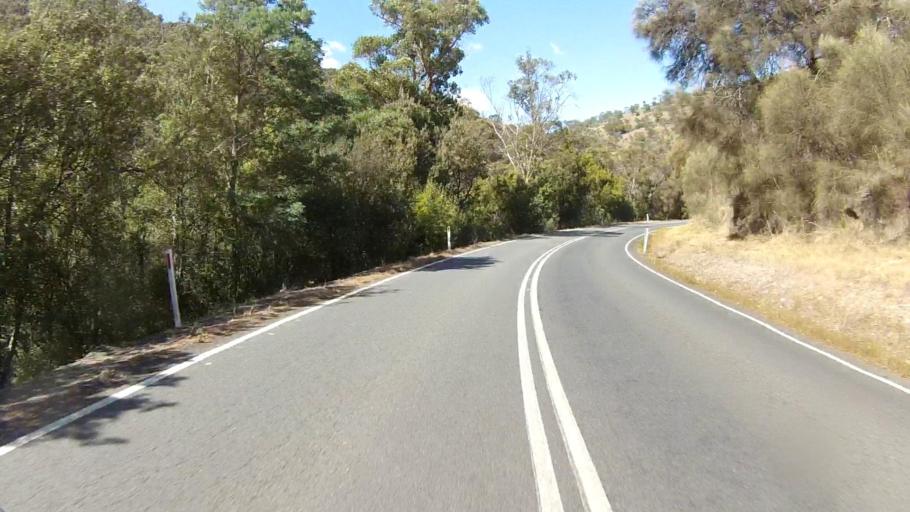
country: AU
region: Tasmania
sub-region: Derwent Valley
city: New Norfolk
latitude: -42.6793
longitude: 146.7663
